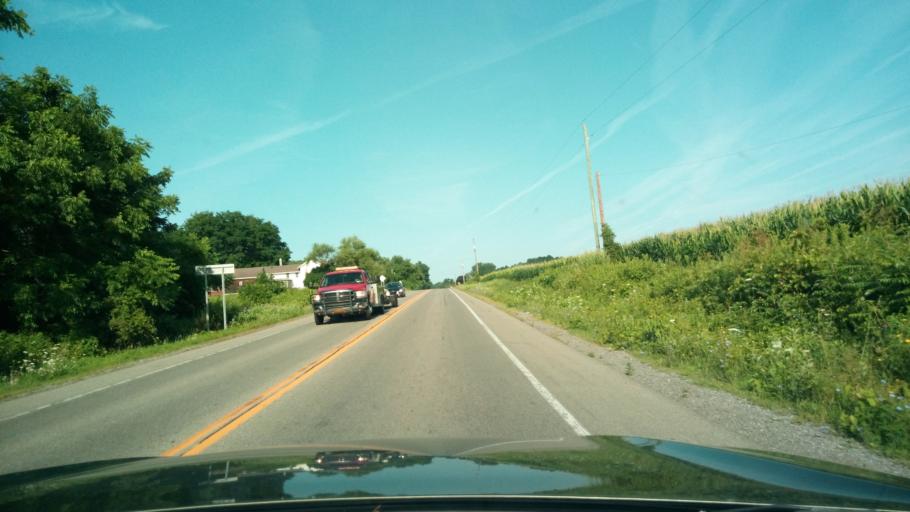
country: US
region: New York
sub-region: Livingston County
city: Mount Morris
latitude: 42.7564
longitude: -77.8855
